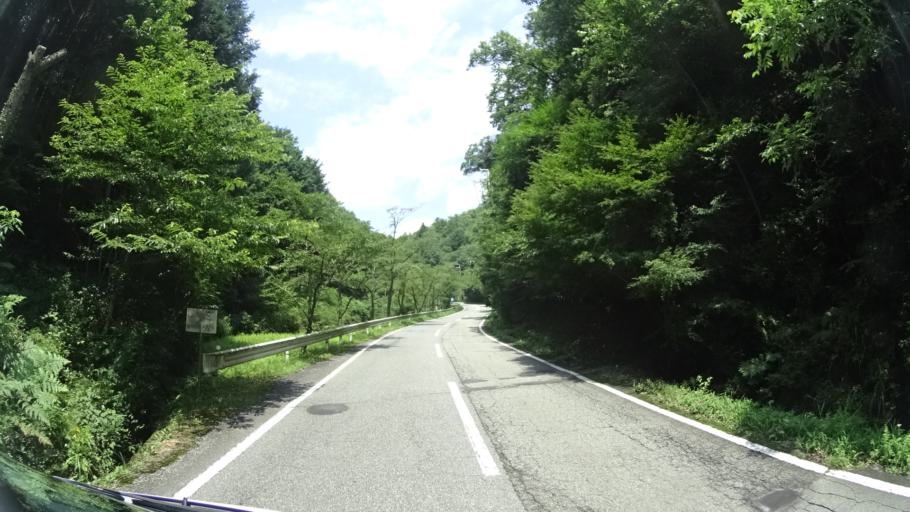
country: JP
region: Hyogo
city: Sasayama
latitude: 35.1714
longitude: 135.2494
